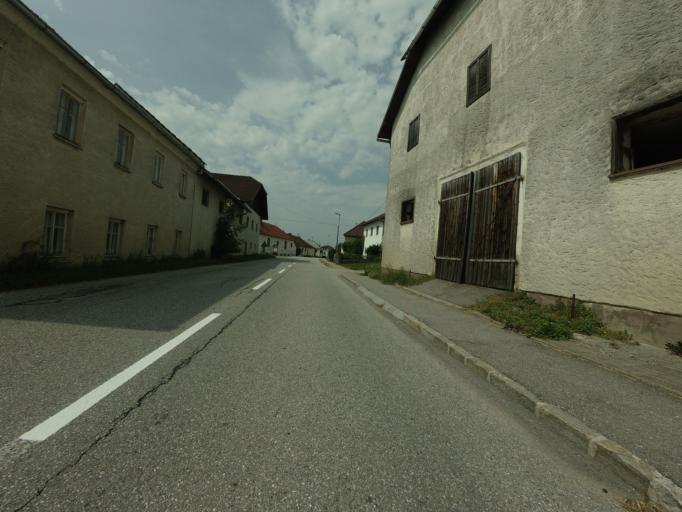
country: AT
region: Upper Austria
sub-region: Politischer Bezirk Urfahr-Umgebung
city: Reichenthal
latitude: 48.5498
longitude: 14.4459
